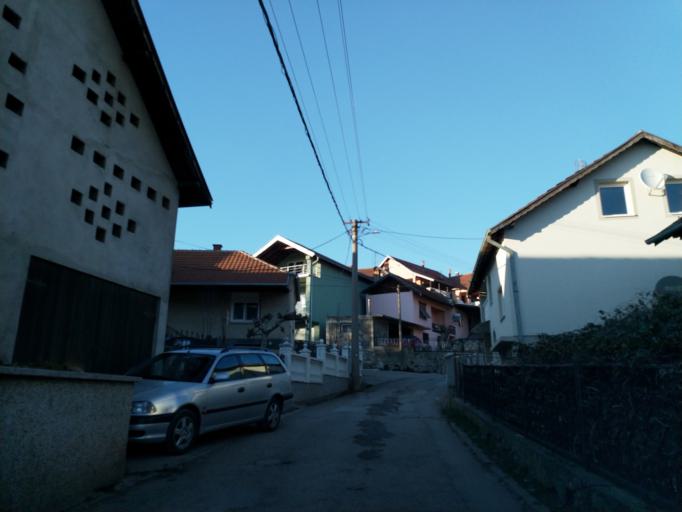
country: RS
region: Central Serbia
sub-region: Pomoravski Okrug
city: Paracin
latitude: 43.9350
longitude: 21.5205
